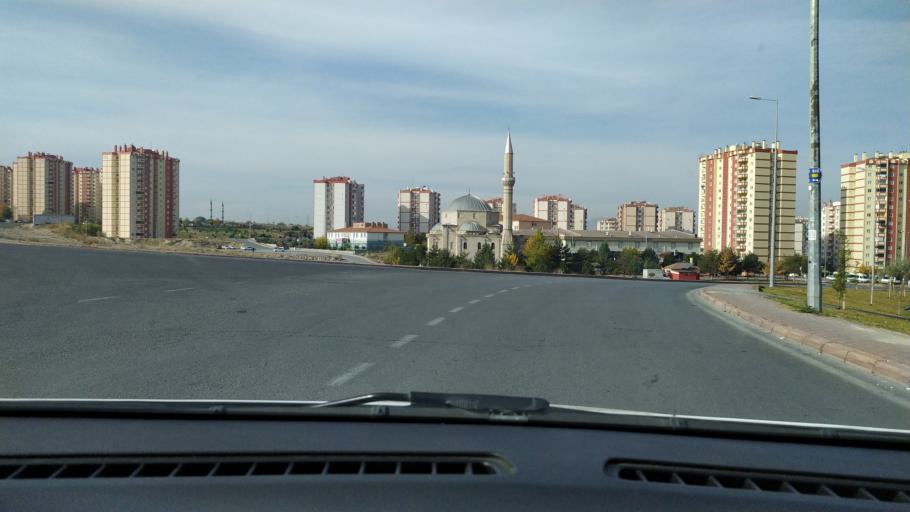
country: TR
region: Kayseri
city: Melikgazi
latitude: 38.7352
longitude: 35.3840
